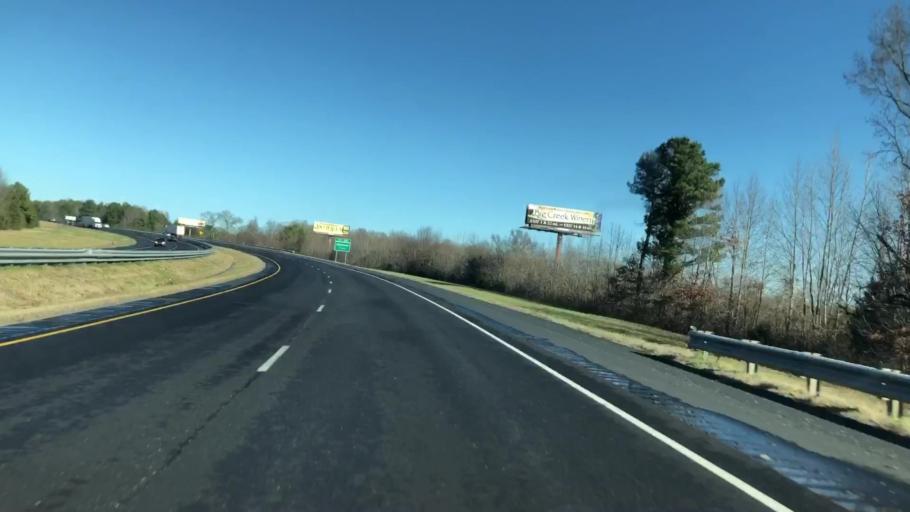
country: US
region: Alabama
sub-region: Limestone County
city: Ardmore
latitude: 34.9014
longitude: -86.9061
